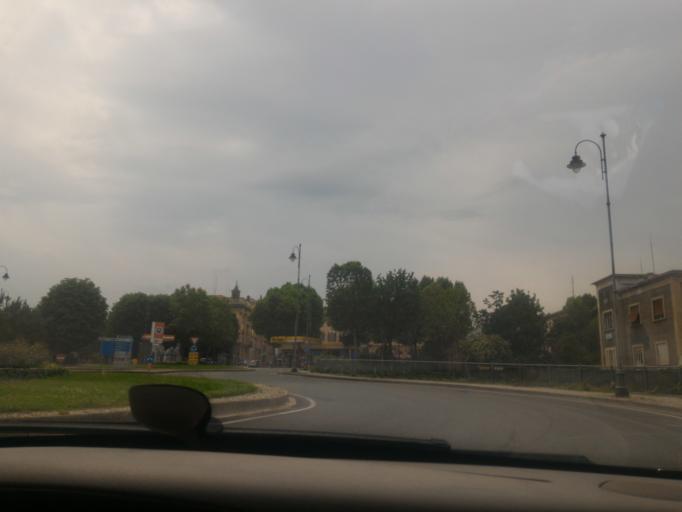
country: IT
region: Piedmont
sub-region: Provincia di Cuneo
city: Cuneo
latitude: 44.3963
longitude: 7.5550
